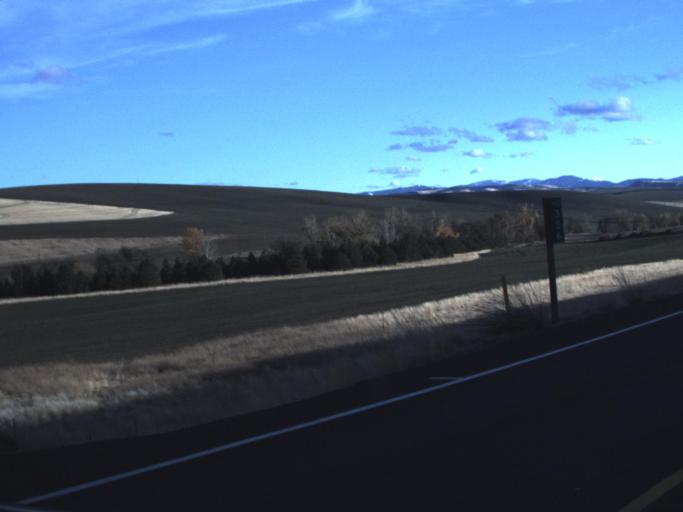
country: US
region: Washington
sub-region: Walla Walla County
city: Waitsburg
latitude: 46.2482
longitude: -118.1464
